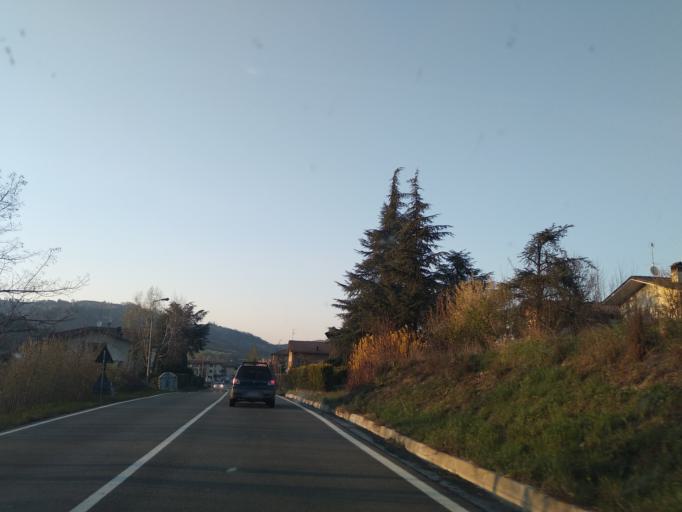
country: IT
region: Emilia-Romagna
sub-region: Provincia di Reggio Emilia
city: Vezzano sul Crostolo
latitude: 44.5582
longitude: 10.5298
